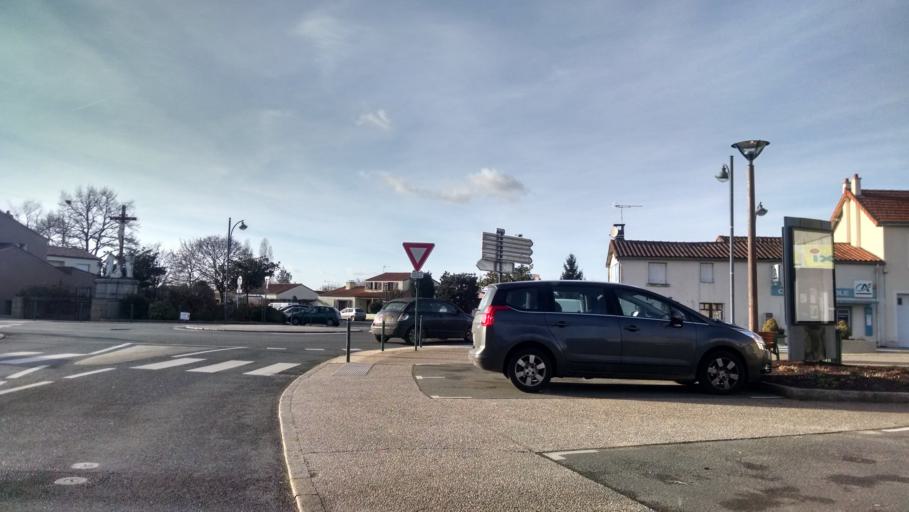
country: FR
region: Pays de la Loire
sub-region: Departement de la Vendee
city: Bouffere
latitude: 46.9602
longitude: -1.3415
